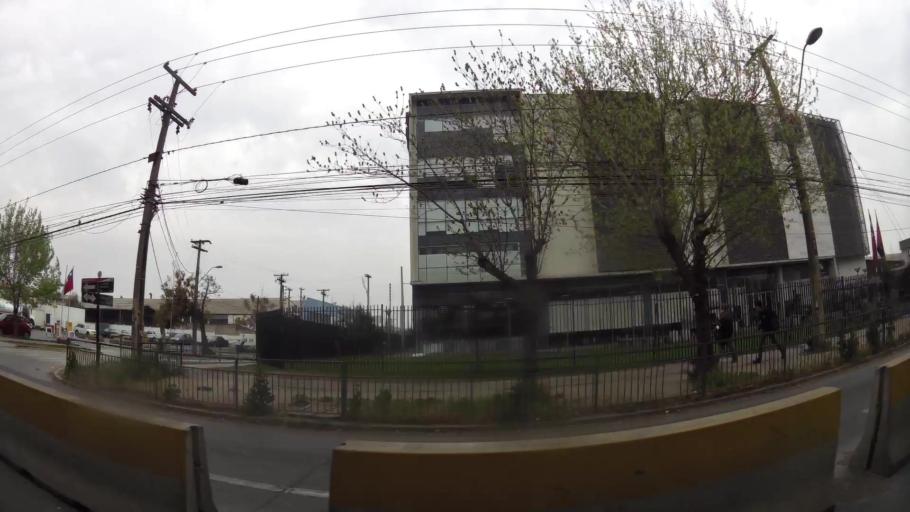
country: CL
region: Santiago Metropolitan
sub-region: Provincia de Santiago
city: Santiago
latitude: -33.4972
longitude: -70.6164
